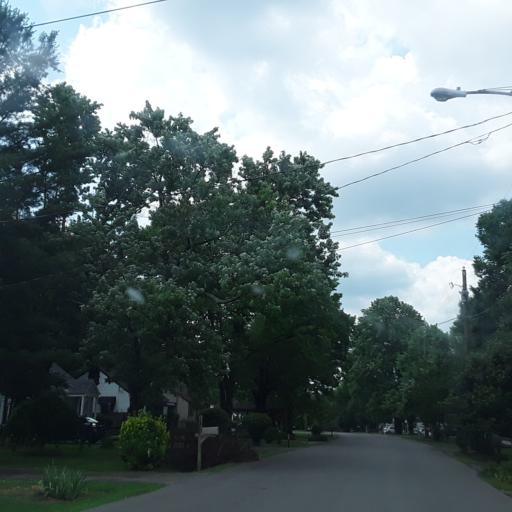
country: US
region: Tennessee
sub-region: Davidson County
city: Oak Hill
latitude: 36.1090
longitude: -86.7347
